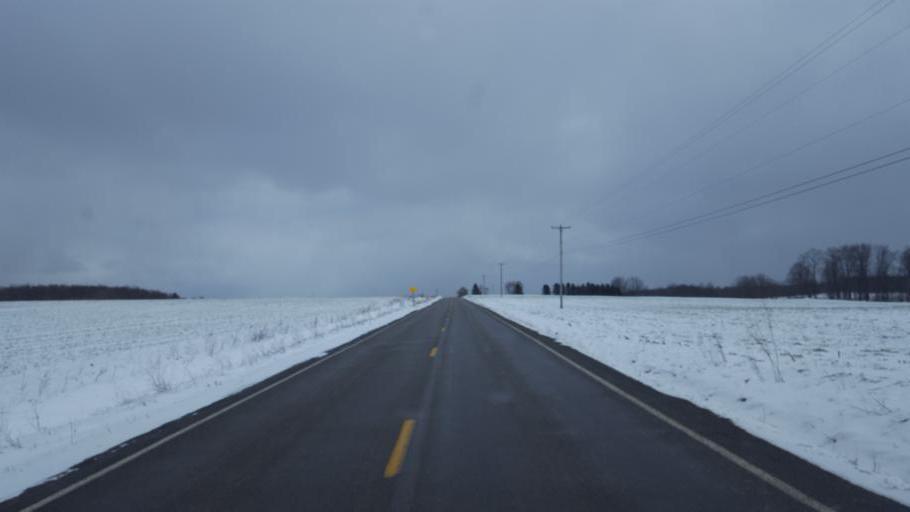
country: US
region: Pennsylvania
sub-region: Mercer County
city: Stoneboro
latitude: 41.4109
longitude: -80.1012
